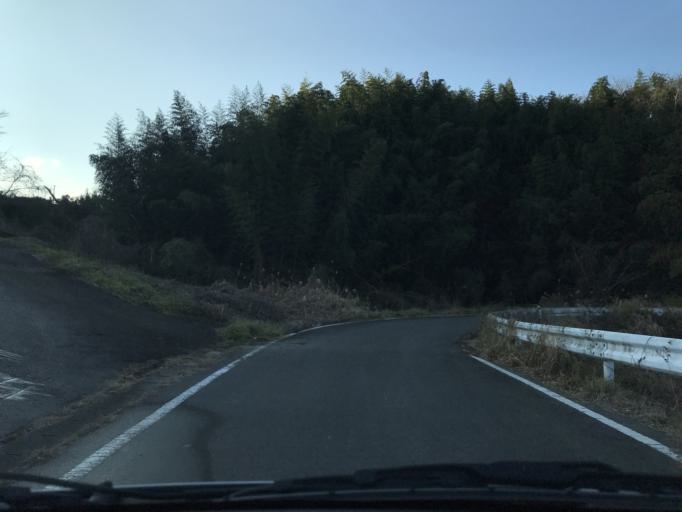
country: JP
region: Miyagi
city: Wakuya
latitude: 38.7011
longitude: 141.1319
